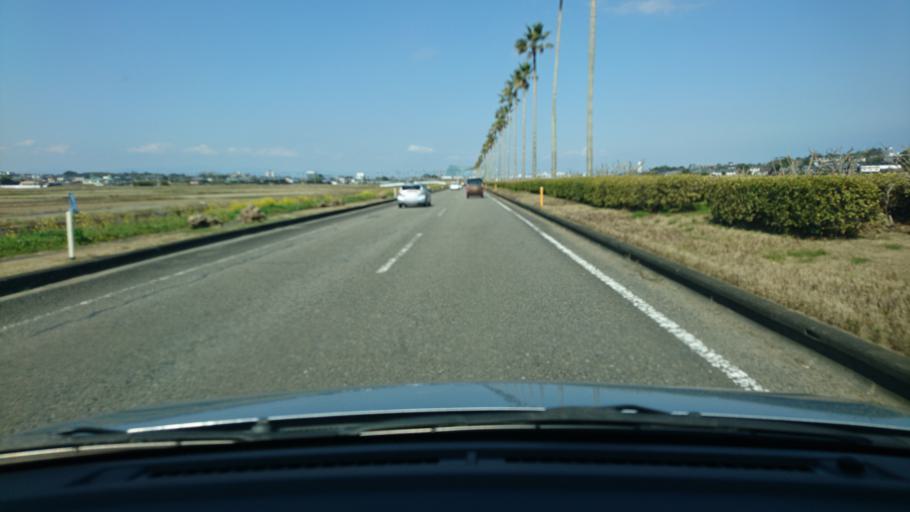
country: JP
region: Miyazaki
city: Miyazaki-shi
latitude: 31.8571
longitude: 131.4429
